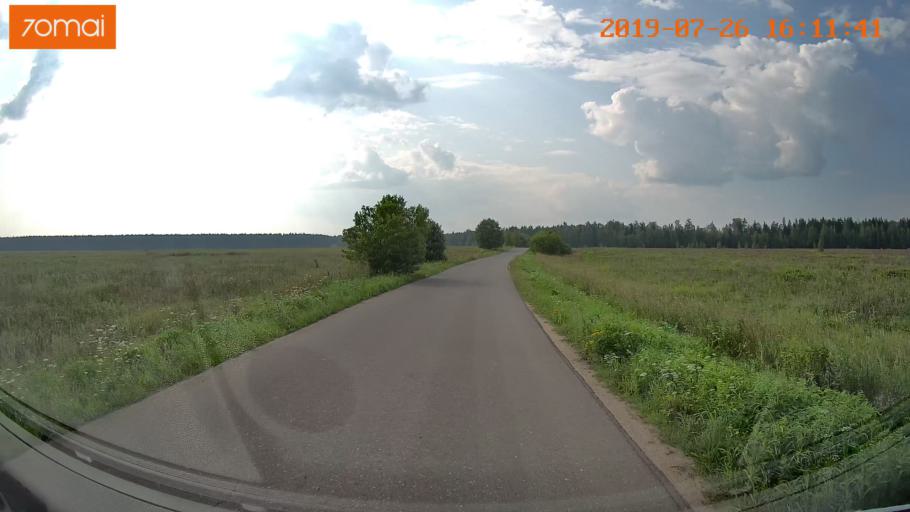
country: RU
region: Ivanovo
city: Bogorodskoye
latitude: 57.0665
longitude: 41.0570
